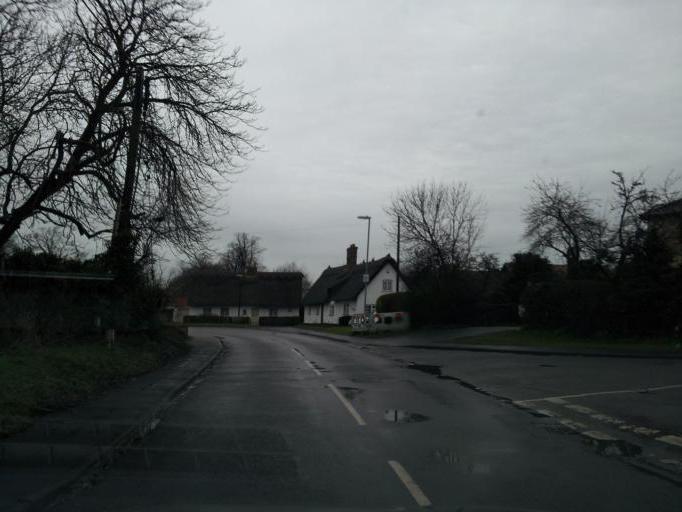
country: GB
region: England
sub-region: Cambridgeshire
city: Bottisham
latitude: 52.2400
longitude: 0.2470
